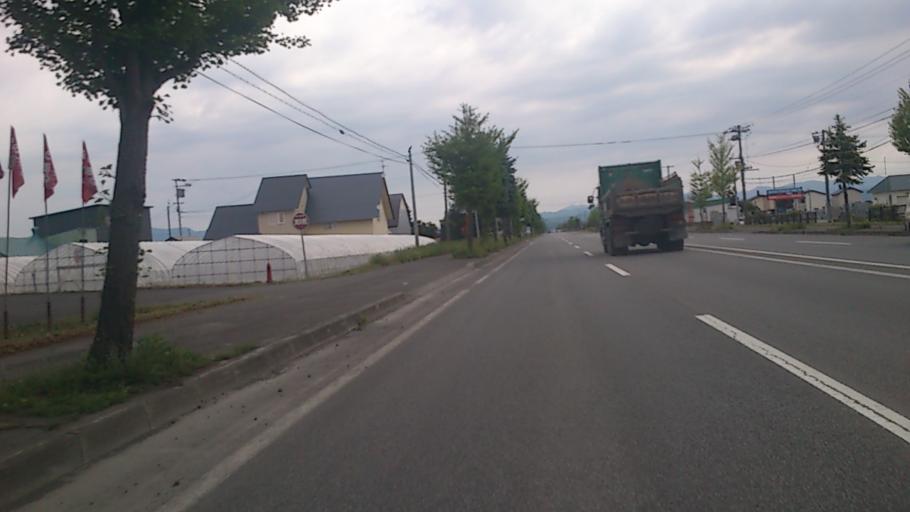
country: JP
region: Hokkaido
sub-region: Asahikawa-shi
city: Asahikawa
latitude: 43.8362
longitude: 142.4748
